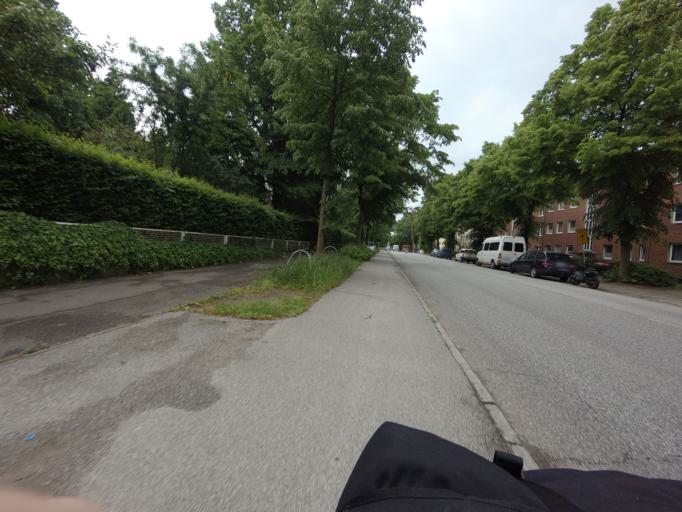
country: DE
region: Mecklenburg-Vorpommern
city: Selmsdorf
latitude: 53.9064
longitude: 10.8034
